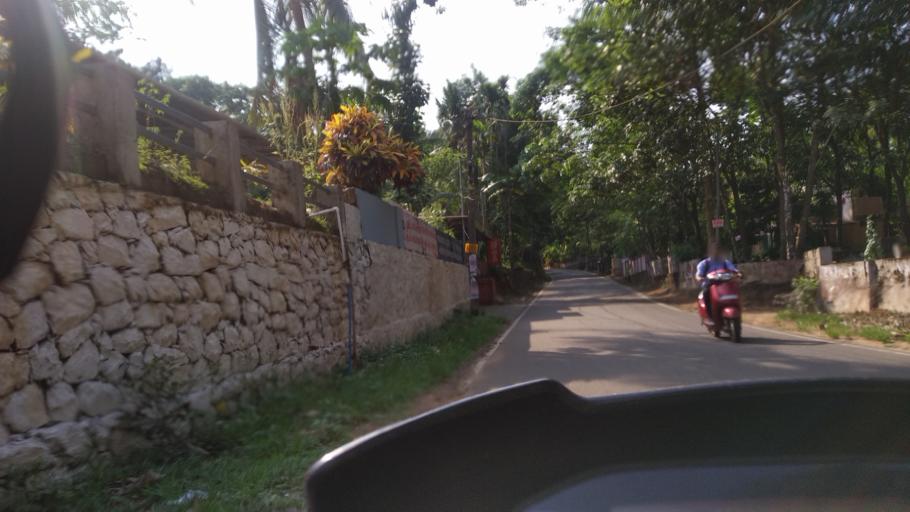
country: IN
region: Kerala
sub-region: Ernakulam
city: Piravam
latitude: 9.8658
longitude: 76.5092
